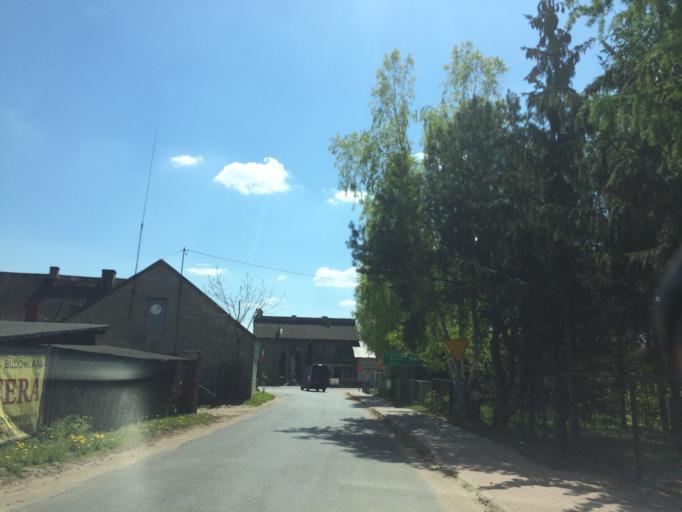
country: PL
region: Warmian-Masurian Voivodeship
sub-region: Powiat nowomiejski
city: Biskupiec
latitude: 53.4448
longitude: 19.3528
